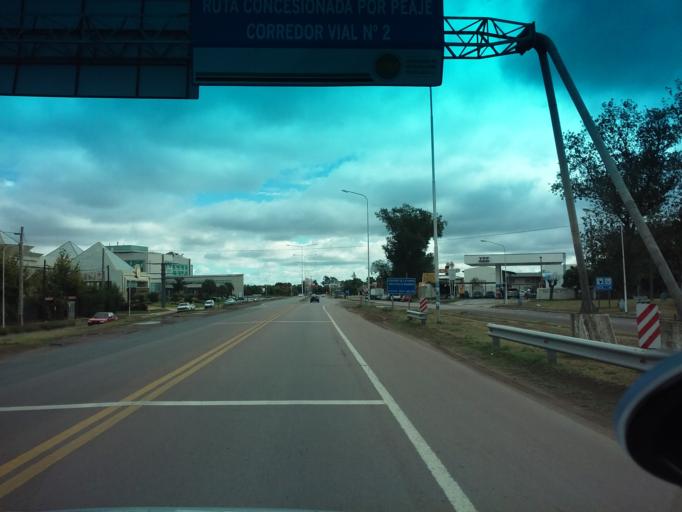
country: AR
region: La Pampa
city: Santa Rosa
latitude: -36.6191
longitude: -64.2665
